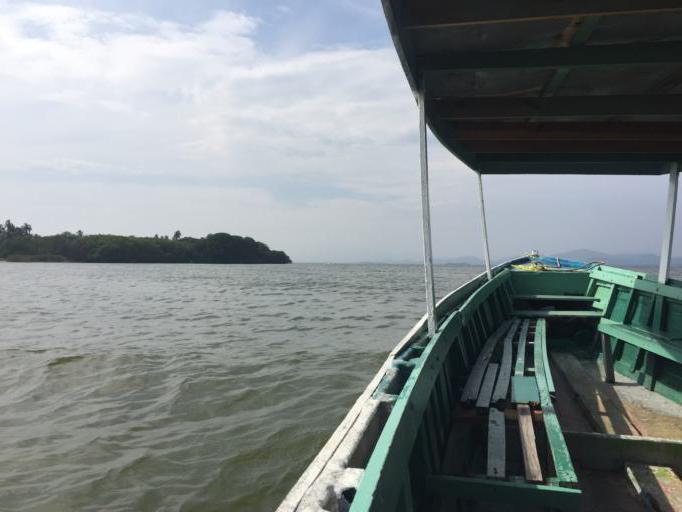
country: MX
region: Guerrero
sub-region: Coyuca de Benitez
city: Colonia Luces en el Mar
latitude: 16.9084
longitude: -99.9741
